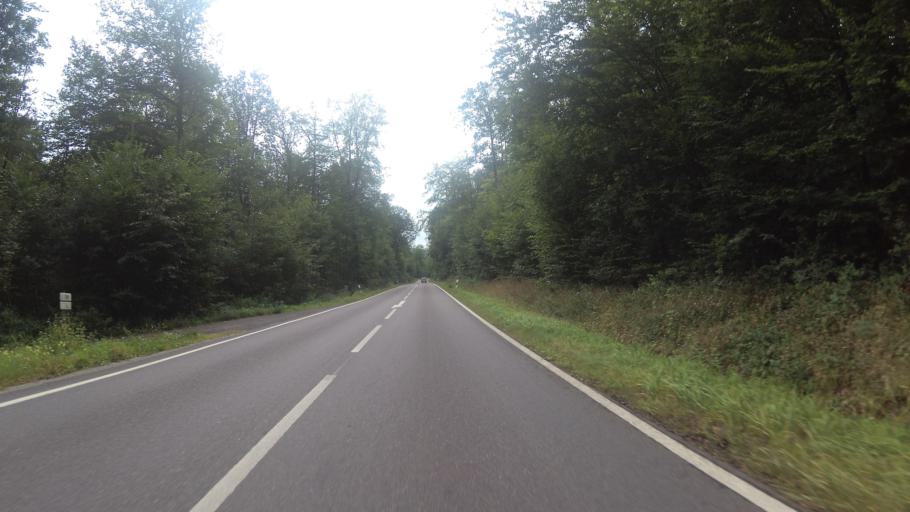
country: DE
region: Saarland
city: Saarbrucken
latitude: 49.2788
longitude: 6.9874
